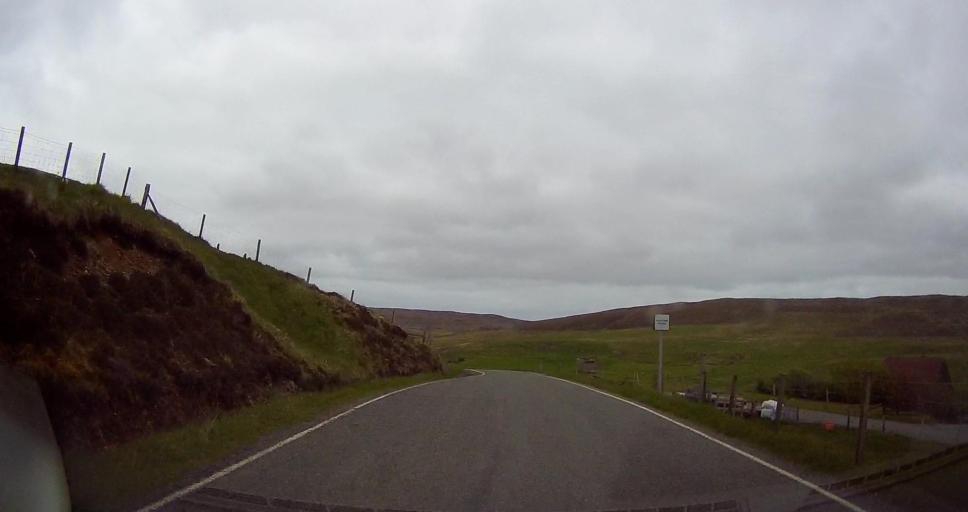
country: GB
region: Scotland
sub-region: Shetland Islands
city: Lerwick
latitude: 60.3431
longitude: -1.2785
